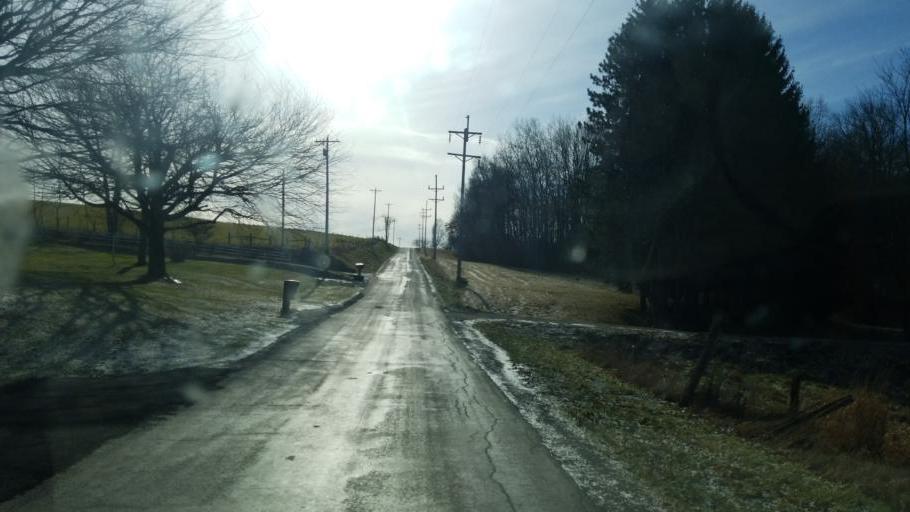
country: US
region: Ohio
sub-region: Sandusky County
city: Bellville
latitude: 40.5783
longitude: -82.5479
